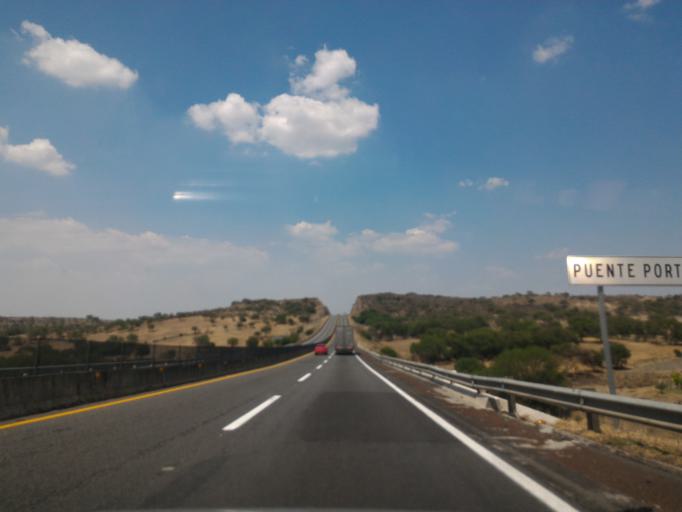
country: MX
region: Jalisco
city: Jalostotitlan
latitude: 21.1336
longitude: -102.4415
